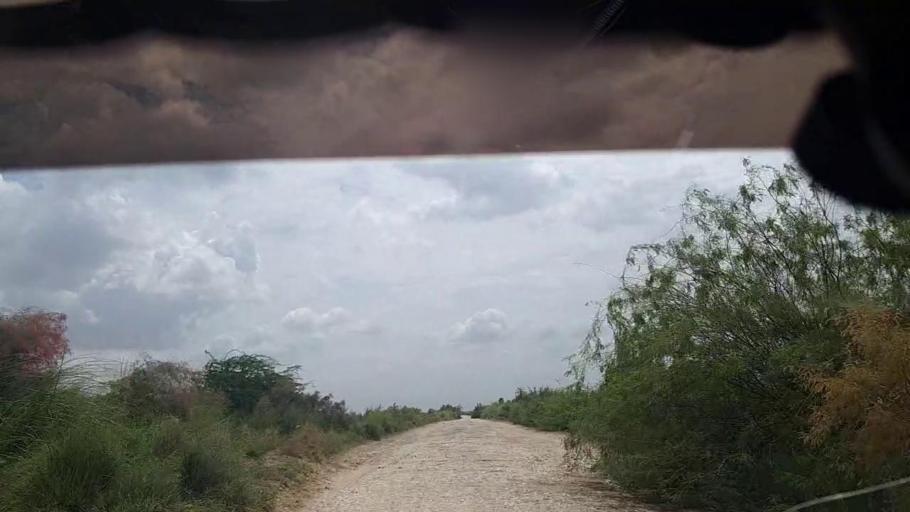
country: PK
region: Sindh
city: Rustam jo Goth
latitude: 28.0566
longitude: 68.9398
